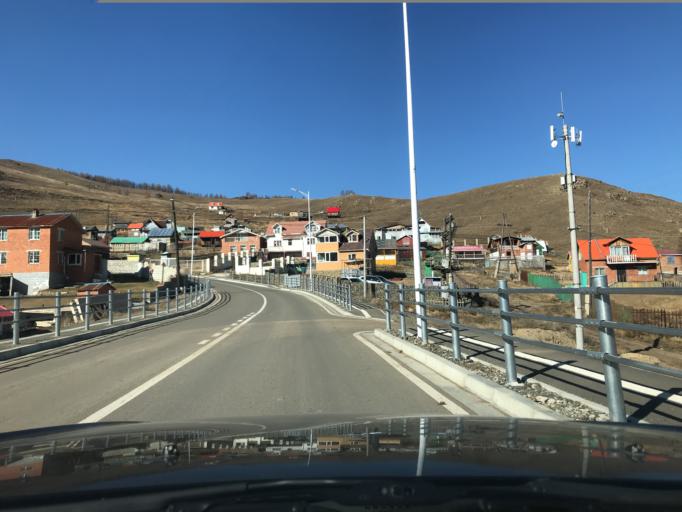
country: MN
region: Ulaanbaatar
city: Ulaanbaatar
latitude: 48.0381
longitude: 106.8982
